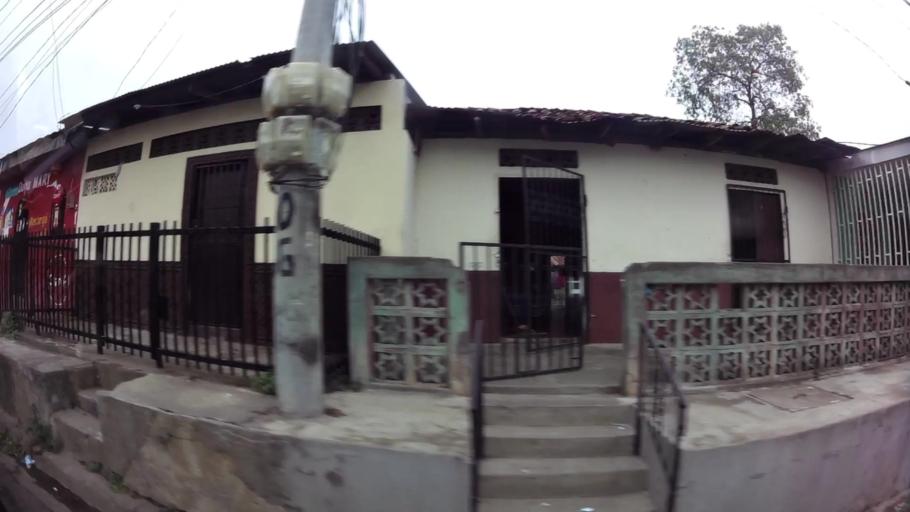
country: NI
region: Leon
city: Leon
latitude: 12.4285
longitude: -86.8800
